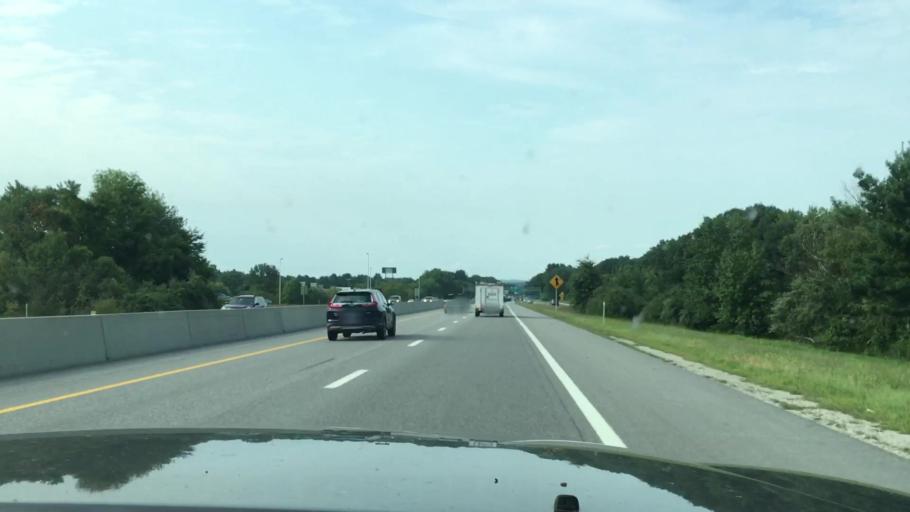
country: US
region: New Hampshire
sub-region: Hillsborough County
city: Bedford
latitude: 42.9523
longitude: -71.4725
